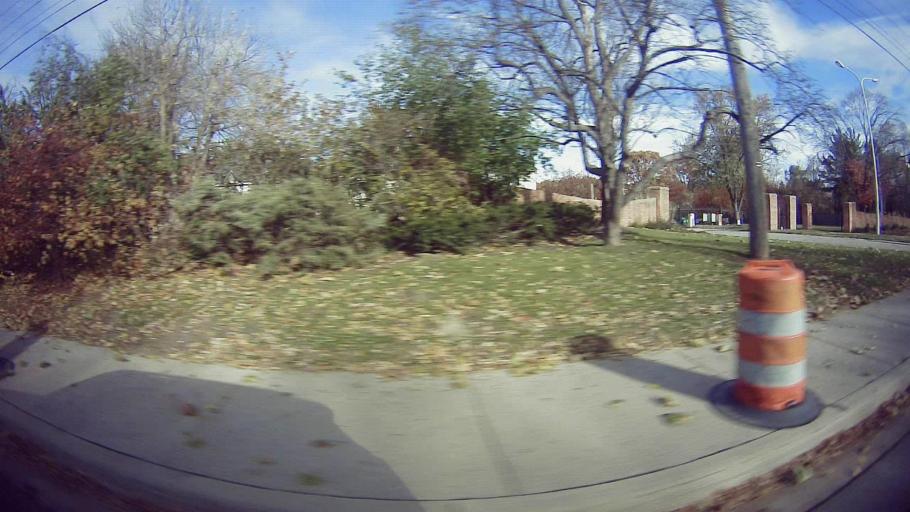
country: US
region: Michigan
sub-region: Oakland County
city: Southfield
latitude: 42.4578
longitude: -83.2639
